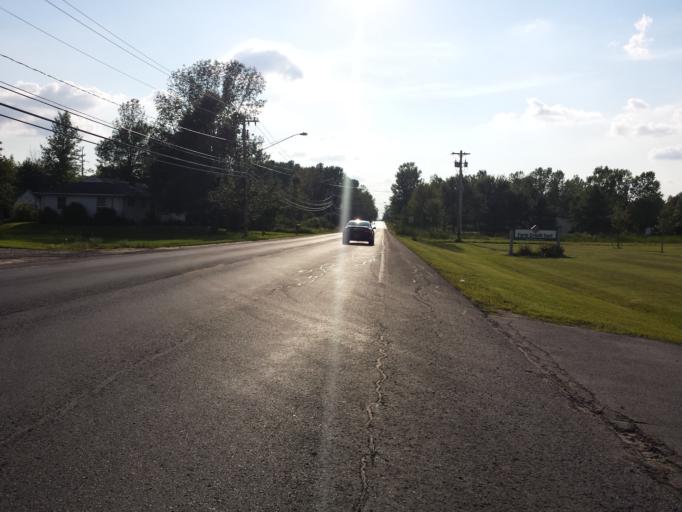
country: US
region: New York
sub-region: St. Lawrence County
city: Potsdam
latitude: 44.6700
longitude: -74.9639
